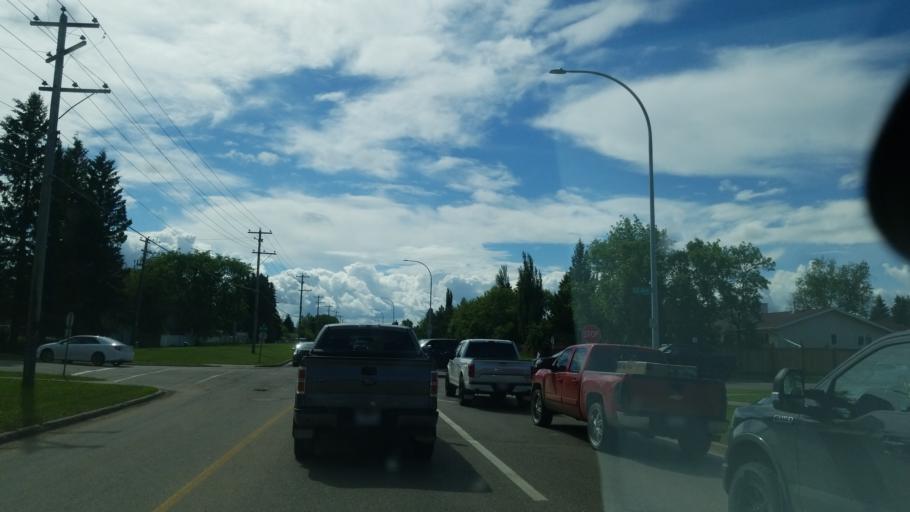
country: CA
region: Saskatchewan
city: Lloydminster
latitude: 53.2708
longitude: -110.0117
